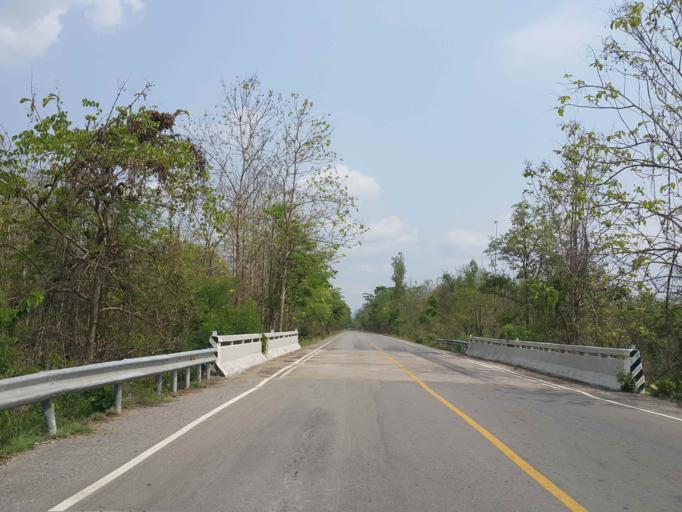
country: TH
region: Sukhothai
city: Thung Saliam
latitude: 17.3734
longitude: 99.4038
